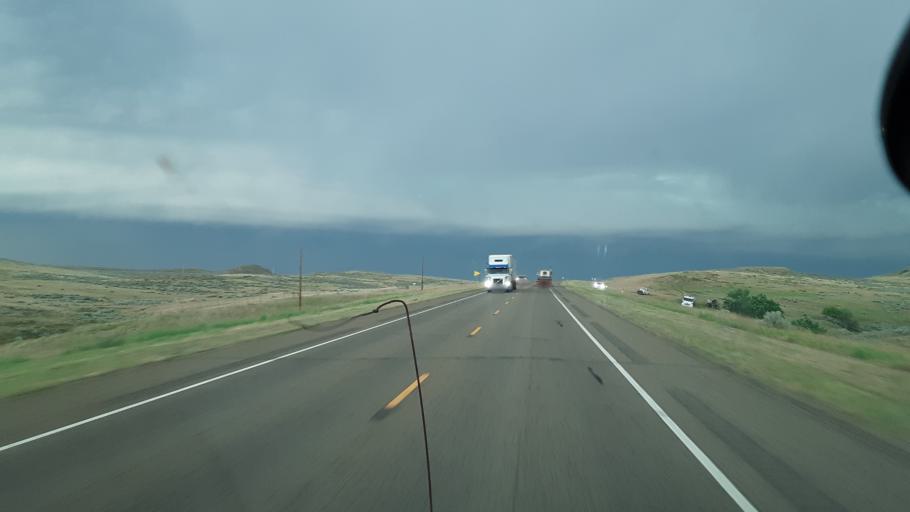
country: US
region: Montana
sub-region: Powder River County
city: Broadus
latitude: 45.3963
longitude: -105.3530
